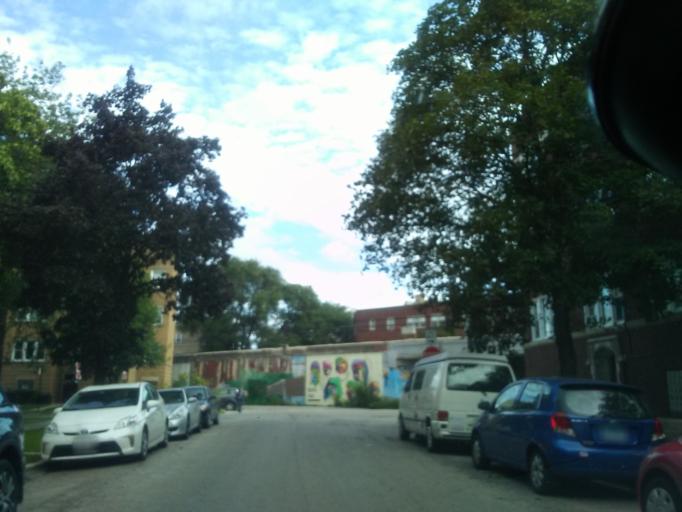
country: US
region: Illinois
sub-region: Cook County
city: Evanston
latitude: 42.0021
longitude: -87.6635
